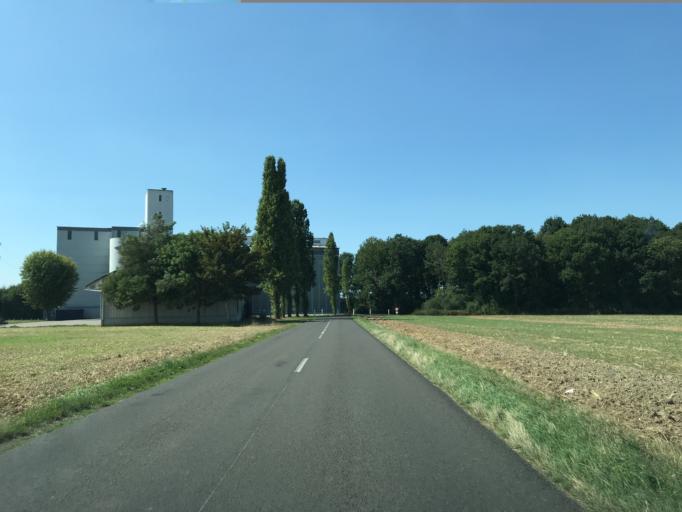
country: FR
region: Haute-Normandie
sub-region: Departement de l'Eure
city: Houlbec-Cocherel
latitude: 49.0938
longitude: 1.3534
